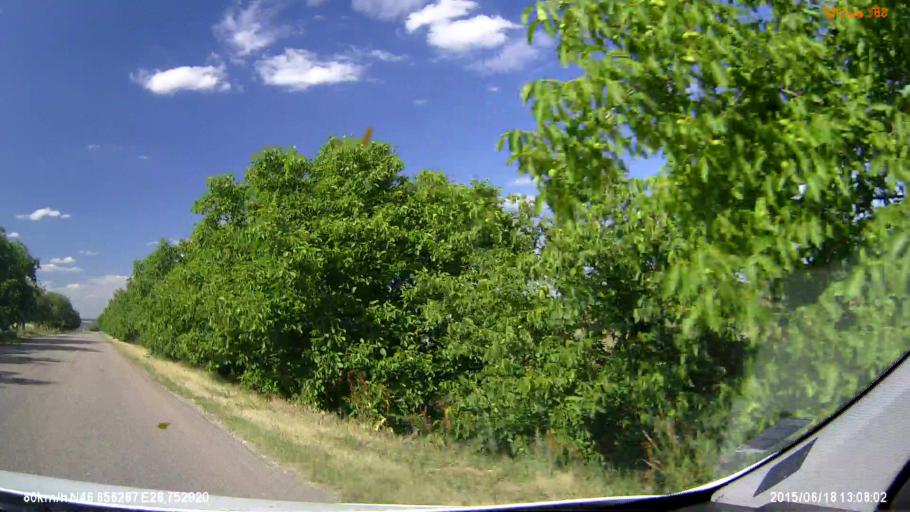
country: MD
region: Cimislia
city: Cimislia
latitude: 46.6563
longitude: 28.7529
